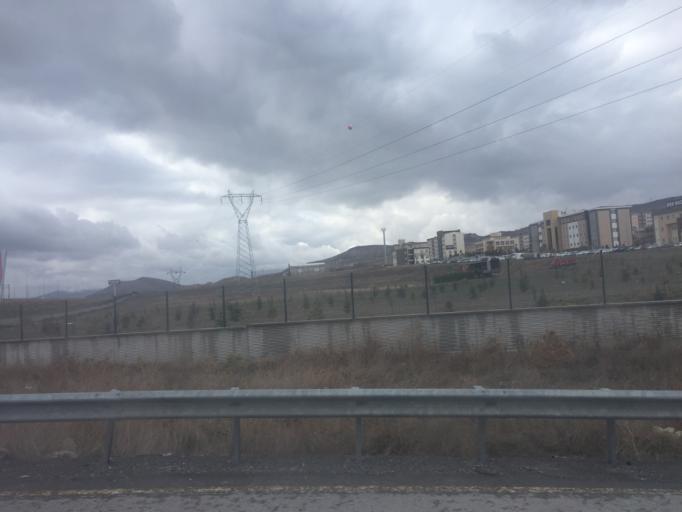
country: TR
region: Kayseri
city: Erkilet
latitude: 38.7835
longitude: 35.4102
